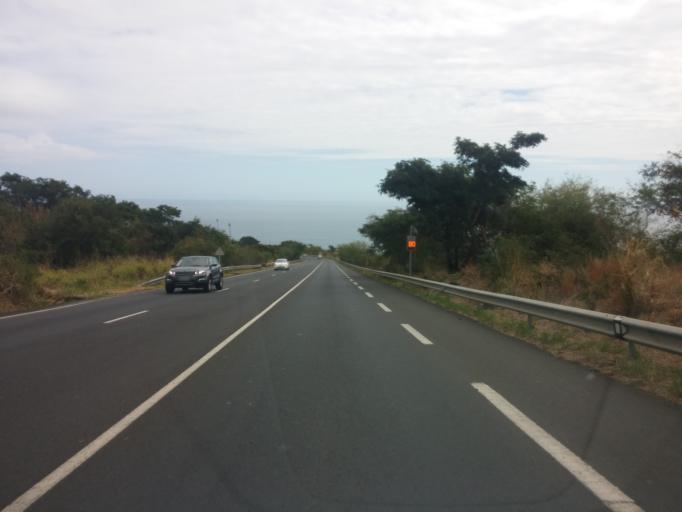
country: RE
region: Reunion
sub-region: Reunion
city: Saint-Paul
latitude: -21.0206
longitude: 55.2722
